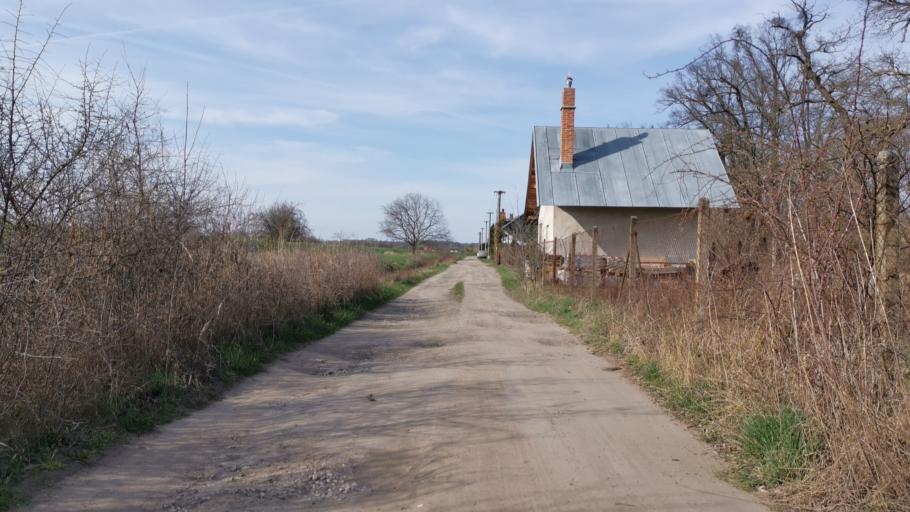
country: CZ
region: South Moravian
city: Tvrdonice
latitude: 48.7193
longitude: 17.0224
